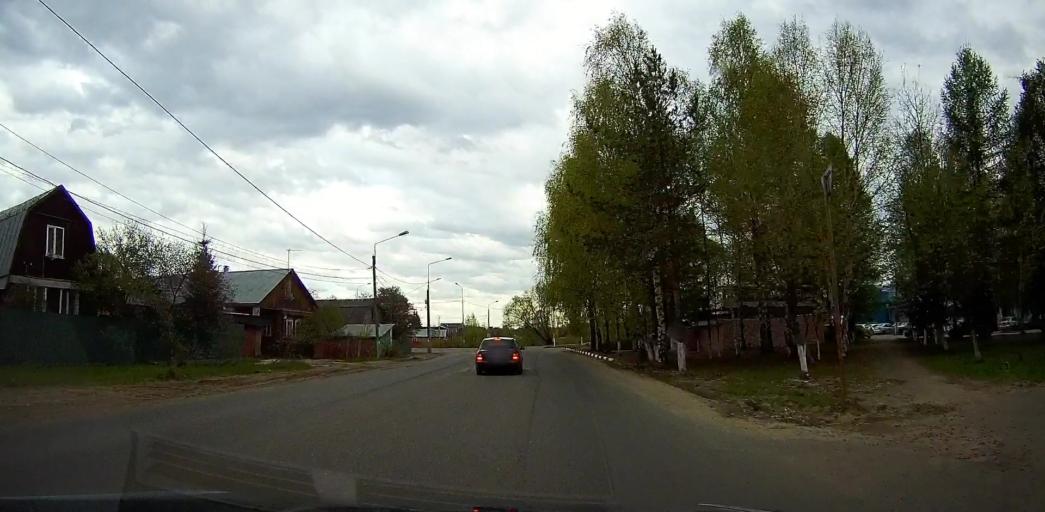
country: RU
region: Moskovskaya
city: Pavlovskiy Posad
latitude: 55.7677
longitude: 38.6958
